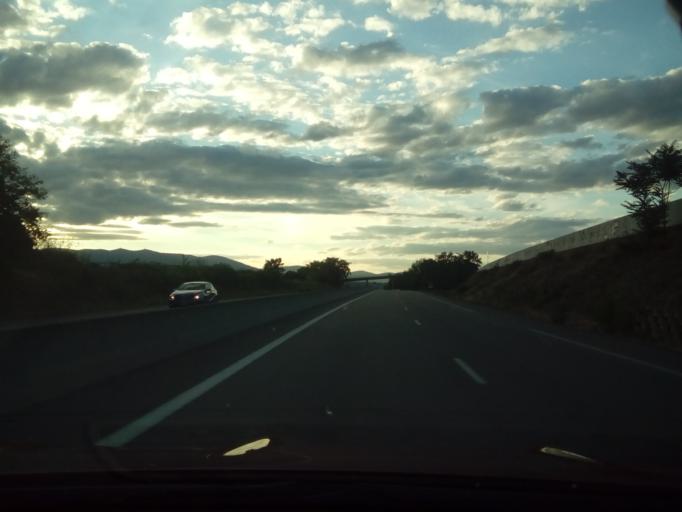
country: FR
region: Rhone-Alpes
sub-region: Departement de l'Isere
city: Chanas
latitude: 45.3030
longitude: 4.8157
